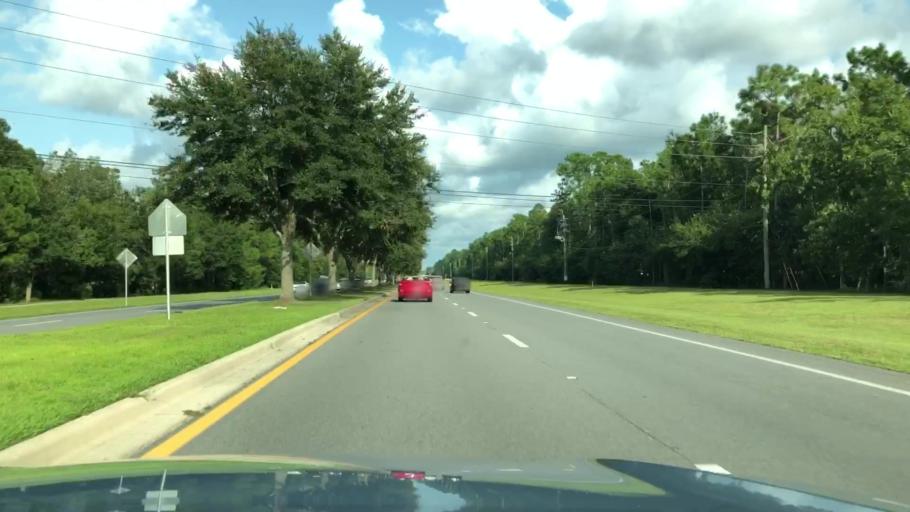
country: US
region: Florida
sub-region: Saint Johns County
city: Fruit Cove
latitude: 30.1109
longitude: -81.5737
